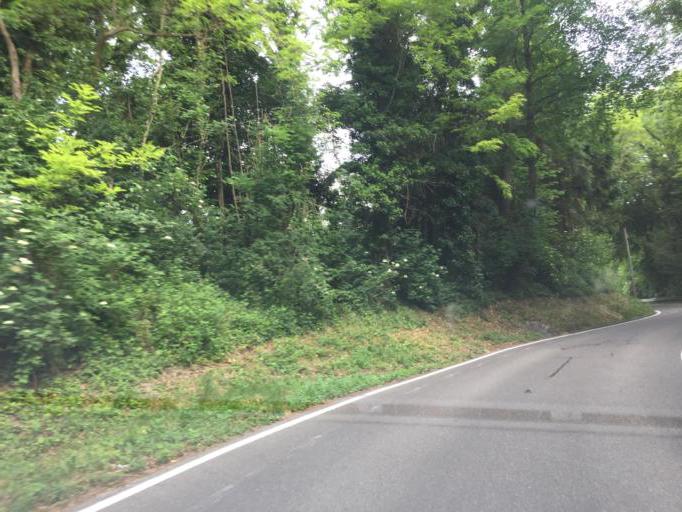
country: CH
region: Zurich
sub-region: Bezirk Andelfingen
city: Dachsen
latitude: 47.6524
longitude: 8.6018
